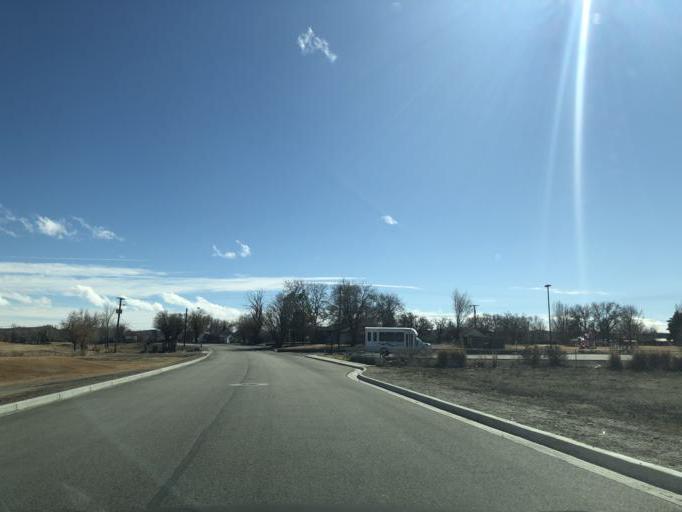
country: US
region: Utah
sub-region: Carbon County
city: East Carbon City
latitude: 38.9942
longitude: -110.1574
